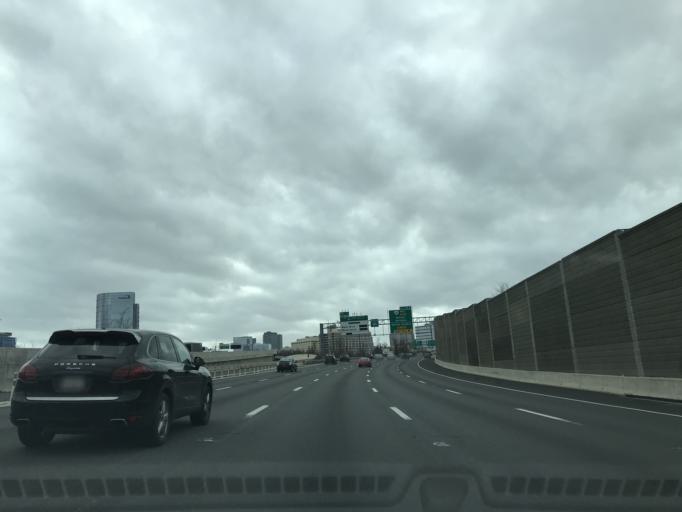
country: US
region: Virginia
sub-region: Fairfax County
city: Pimmit Hills
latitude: 38.9380
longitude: -77.2057
